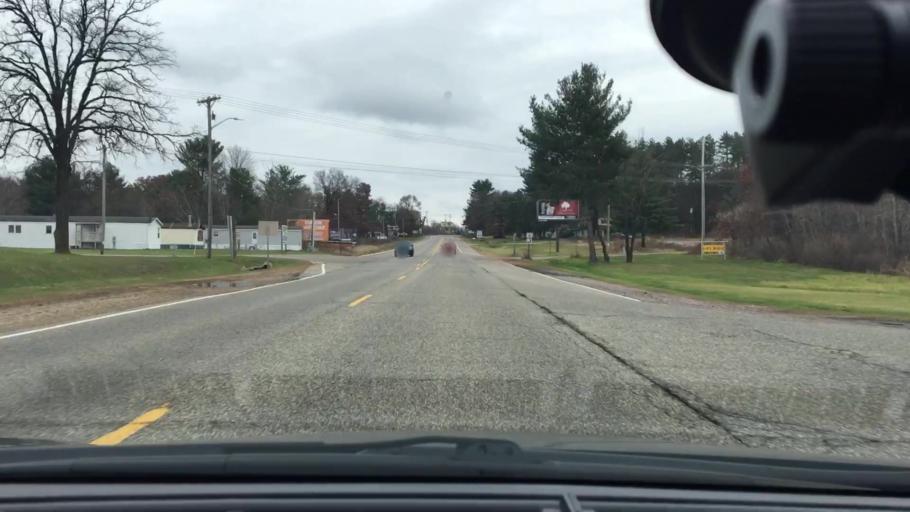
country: US
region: Wisconsin
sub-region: Columbia County
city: Wisconsin Dells
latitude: 43.6338
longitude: -89.7916
